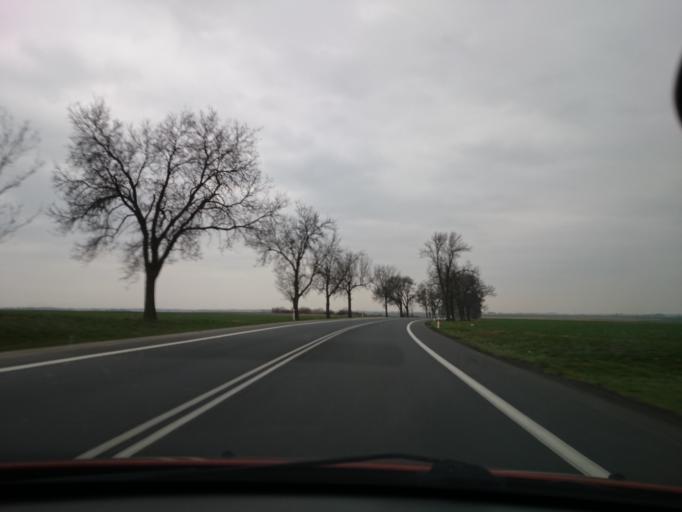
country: PL
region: Opole Voivodeship
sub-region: Powiat nyski
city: Sidzina
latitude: 50.5612
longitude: 17.4304
